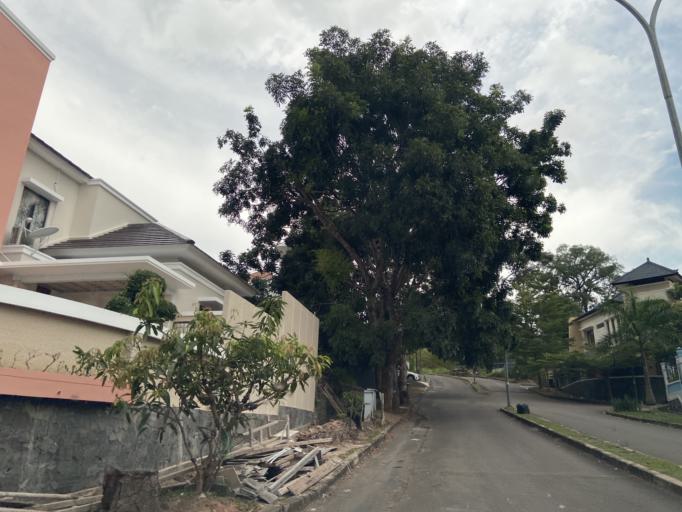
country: SG
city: Singapore
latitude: 1.1017
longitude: 104.0272
